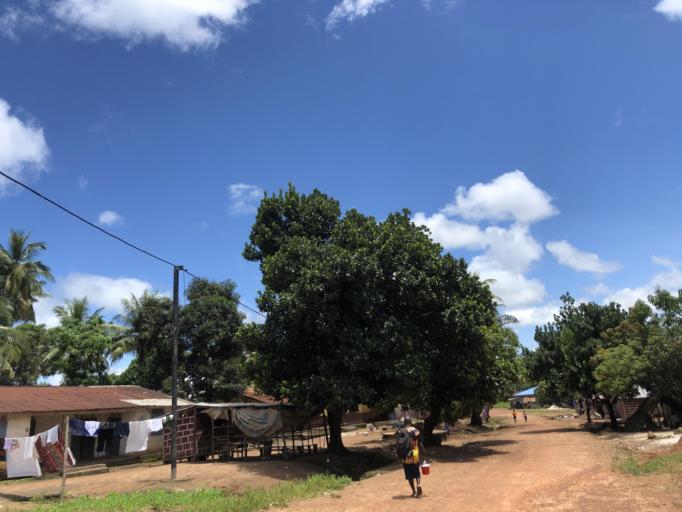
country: SL
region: Northern Province
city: Makeni
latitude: 8.8673
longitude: -12.1258
